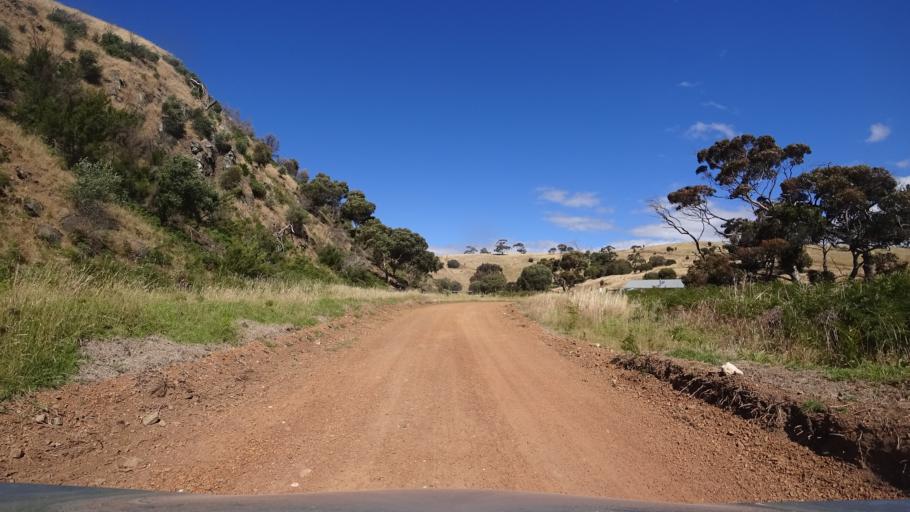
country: AU
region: South Australia
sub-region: Kangaroo Island
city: Kingscote
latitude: -35.6805
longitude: 136.9721
